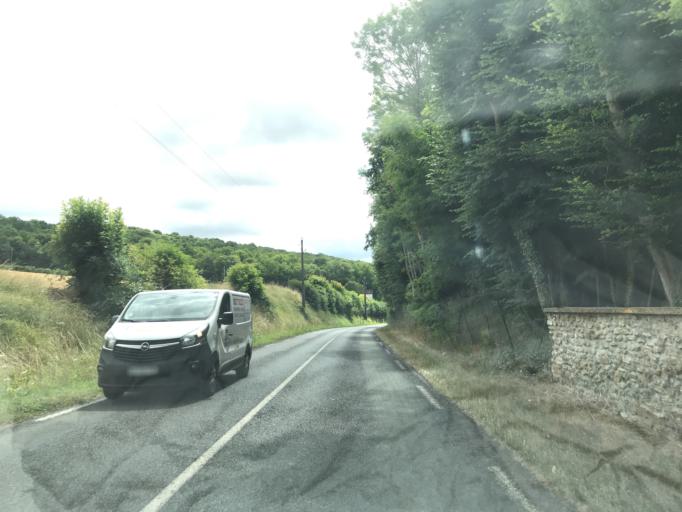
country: FR
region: Haute-Normandie
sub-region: Departement de l'Eure
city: Houlbec-Cocherel
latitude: 49.0612
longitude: 1.3305
